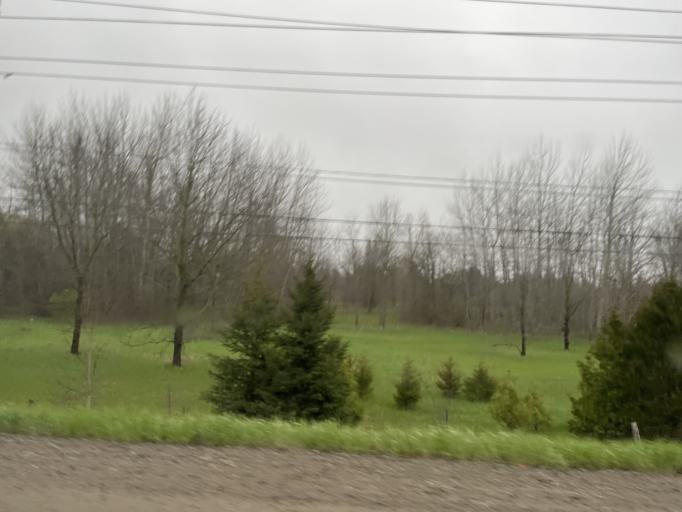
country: CA
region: Ontario
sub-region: Wellington County
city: Guelph
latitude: 43.5465
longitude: -80.2164
